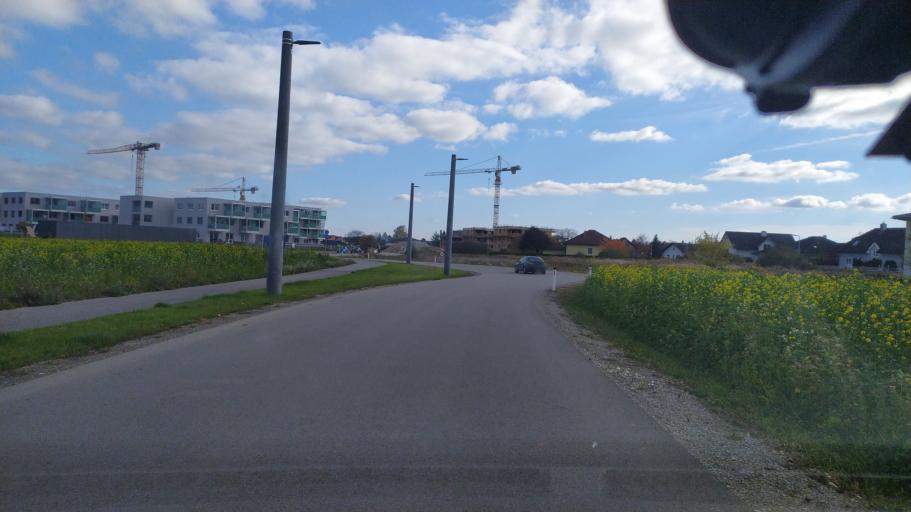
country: AT
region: Upper Austria
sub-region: Politischer Bezirk Urfahr-Umgebung
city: Steyregg
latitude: 48.2553
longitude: 14.3656
